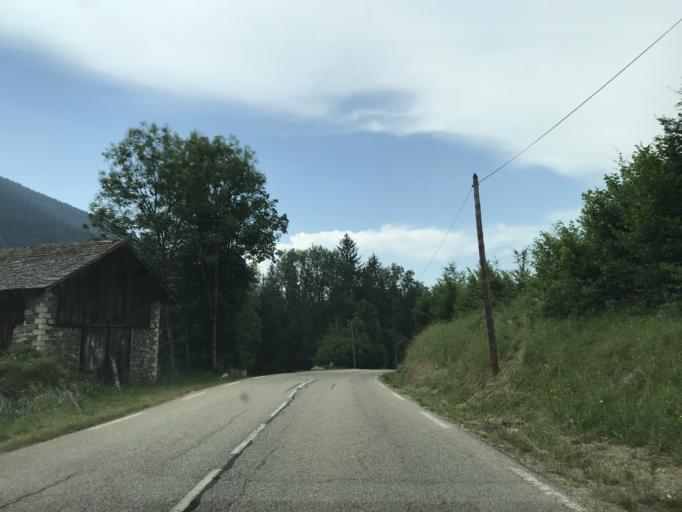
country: FR
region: Rhone-Alpes
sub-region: Departement de l'Isere
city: Allevard
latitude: 45.3258
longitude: 6.0902
